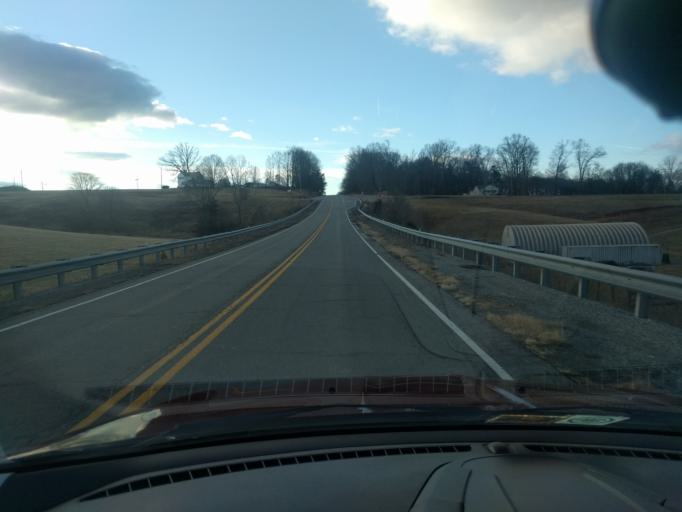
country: US
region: Virginia
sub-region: City of Bedford
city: Bedford
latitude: 37.2769
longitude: -79.5529
